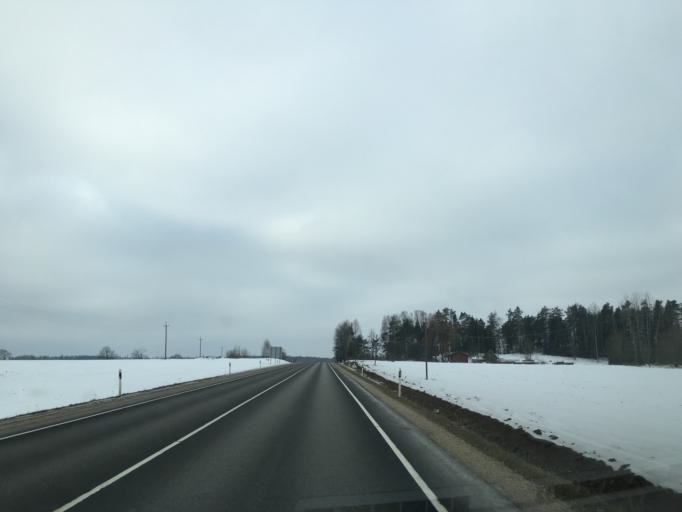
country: EE
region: Tartu
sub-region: Elva linn
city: Elva
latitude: 58.1849
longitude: 26.3458
